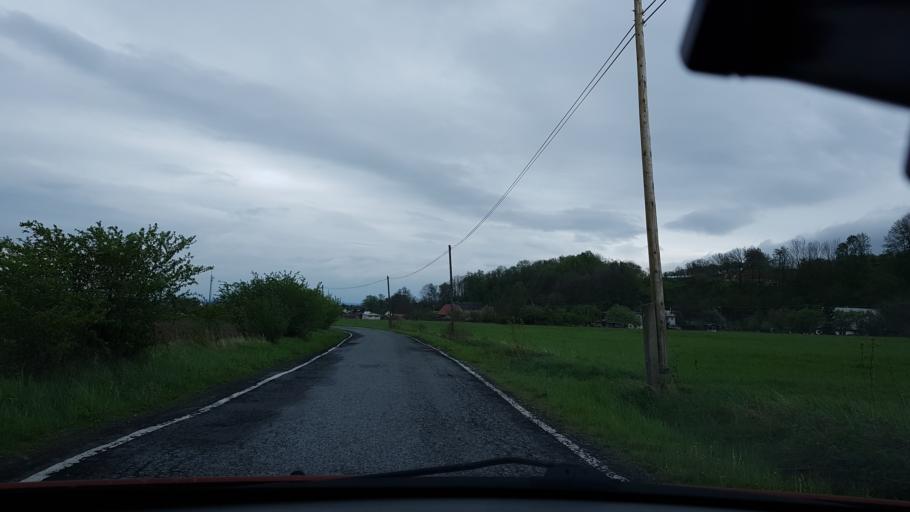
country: PL
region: Lower Silesian Voivodeship
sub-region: Powiat zabkowicki
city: Zloty Stok
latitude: 50.4433
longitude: 16.9064
